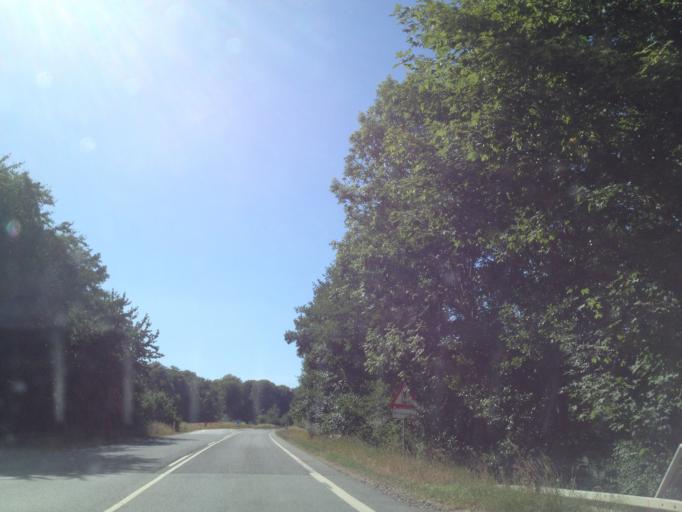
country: DK
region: Capital Region
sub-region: Fredensborg Kommune
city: Fredensborg
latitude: 56.0425
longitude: 12.3792
